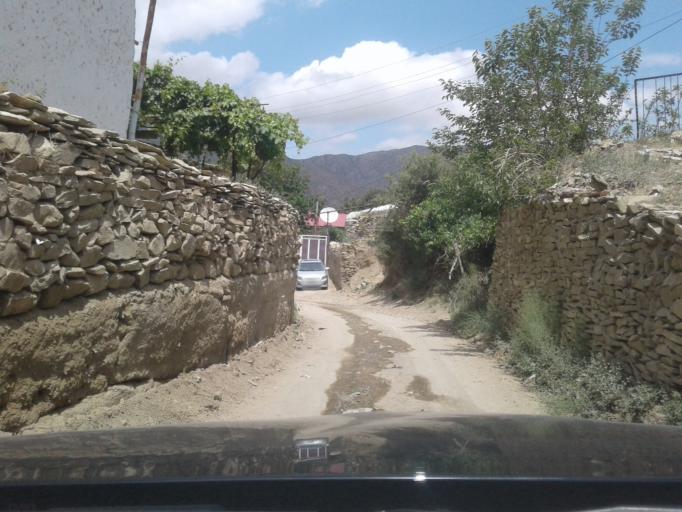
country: TM
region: Ahal
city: Baharly
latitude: 38.4736
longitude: 57.0378
